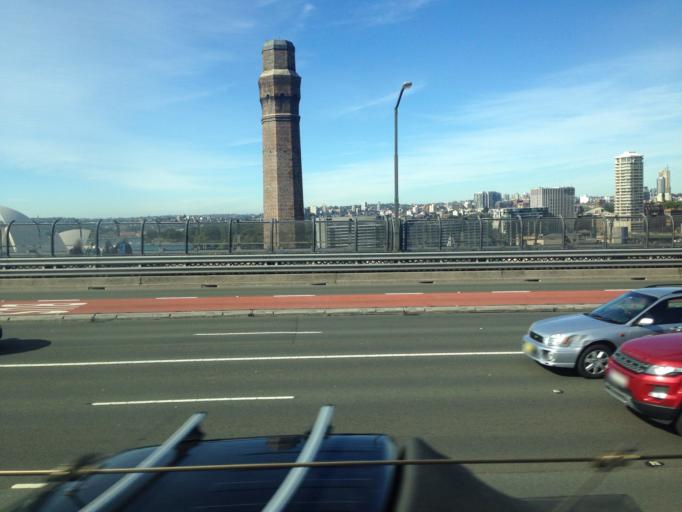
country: AU
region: New South Wales
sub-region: North Sydney
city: Milsons Point
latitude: -33.8564
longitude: 151.2080
